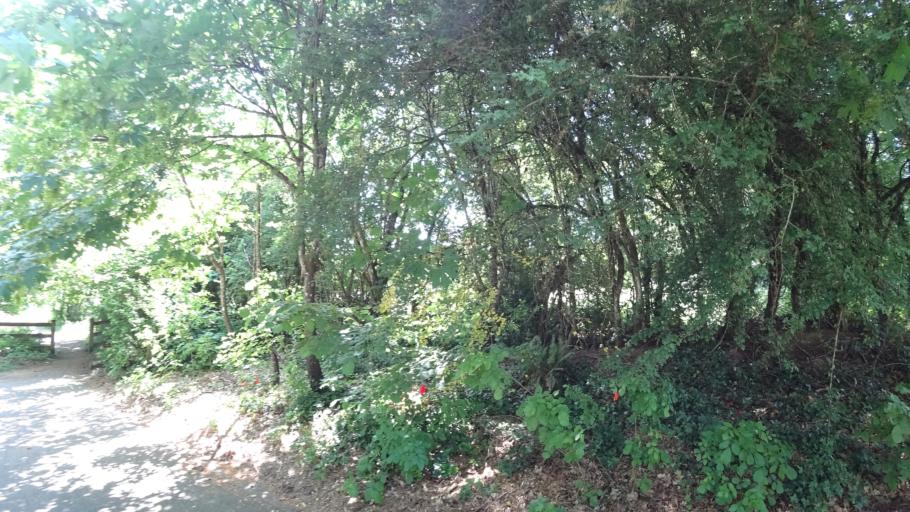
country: US
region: Oregon
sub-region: Clackamas County
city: Lake Oswego
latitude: 45.4275
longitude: -122.6887
